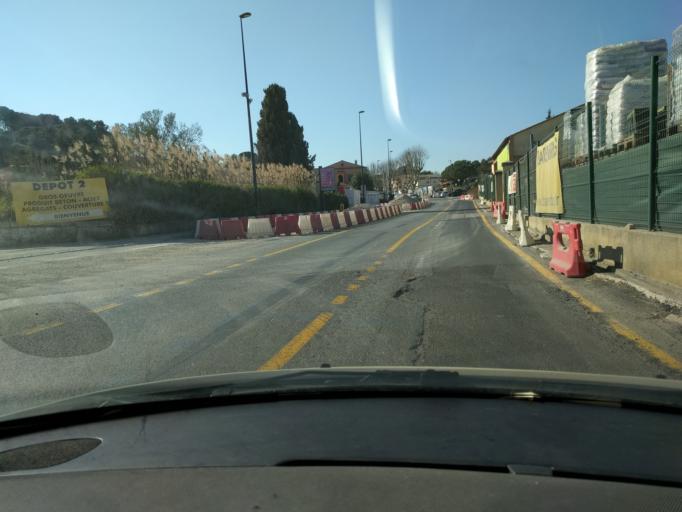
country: FR
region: Provence-Alpes-Cote d'Azur
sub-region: Departement des Alpes-Maritimes
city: Mougins
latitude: 43.6032
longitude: 6.9869
